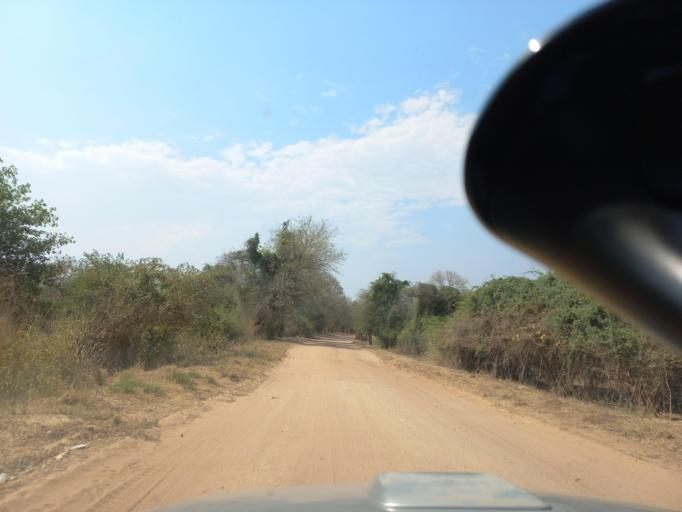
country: ZW
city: Chirundu
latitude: -15.9299
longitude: 28.8715
